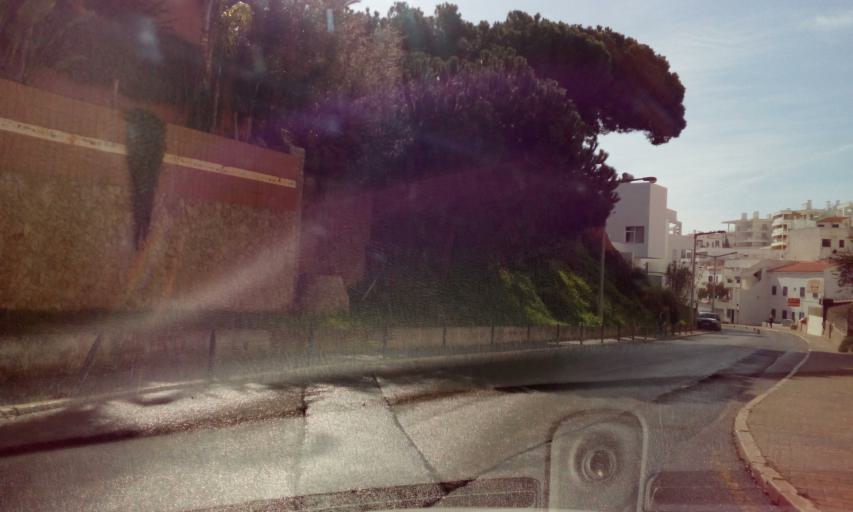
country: PT
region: Faro
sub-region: Loule
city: Boliqueime
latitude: 37.0918
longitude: -8.1885
